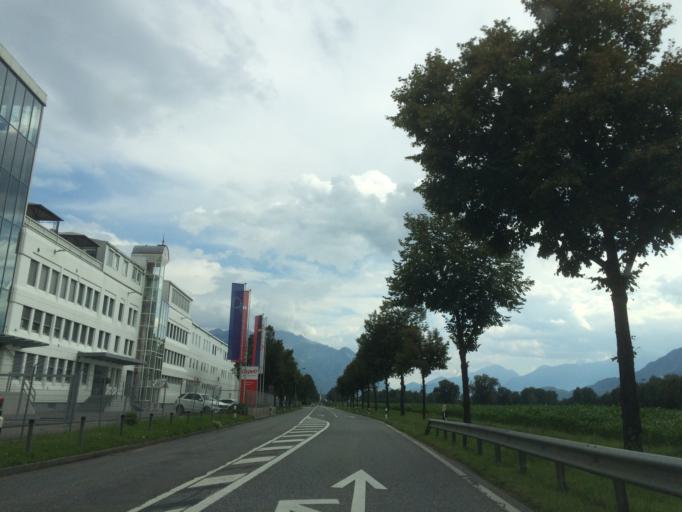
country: CH
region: Saint Gallen
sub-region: Wahlkreis Werdenberg
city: Haag (Rheintal)
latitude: 47.2002
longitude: 9.5011
